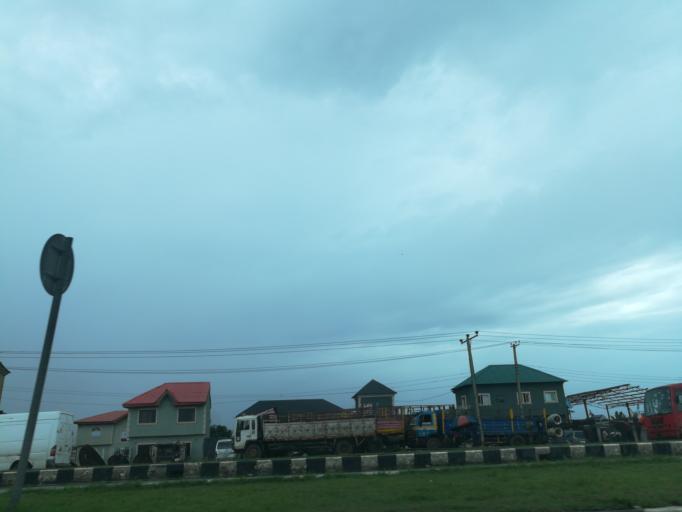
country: NG
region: Lagos
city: Ojota
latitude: 6.6062
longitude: 3.4073
